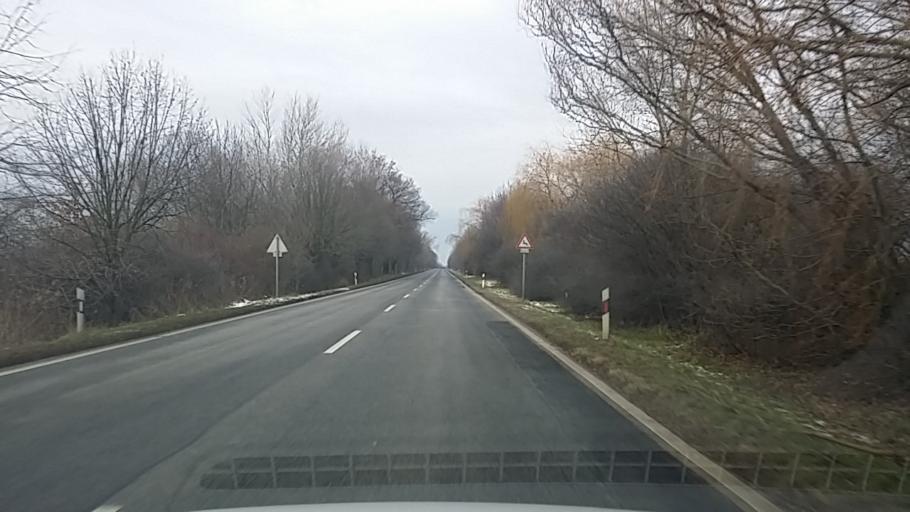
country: HU
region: Komarom-Esztergom
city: Kisber
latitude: 47.4686
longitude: 18.0840
